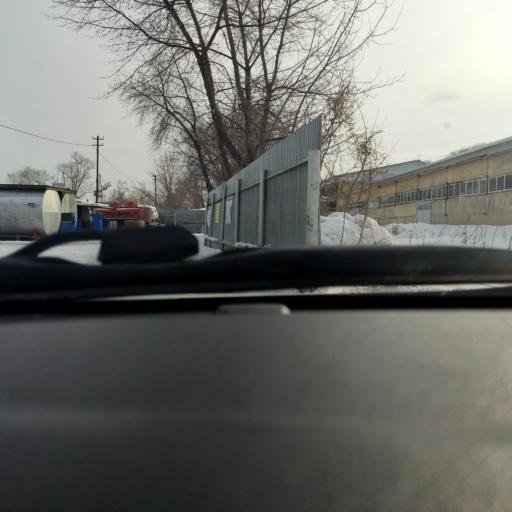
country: RU
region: Bashkortostan
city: Ufa
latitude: 54.8038
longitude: 56.0745
